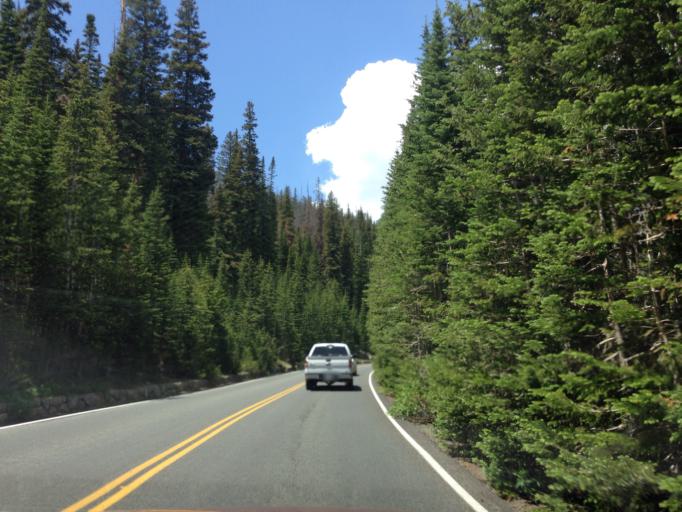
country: US
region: Colorado
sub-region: Larimer County
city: Estes Park
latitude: 40.3857
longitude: -105.6657
